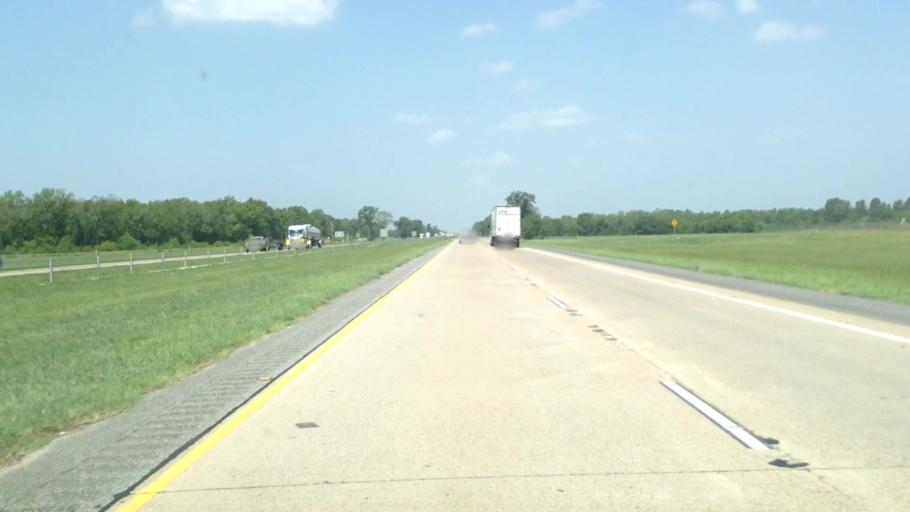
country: US
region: Louisiana
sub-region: Ouachita Parish
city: Lakeshore
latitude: 32.4892
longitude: -91.9913
